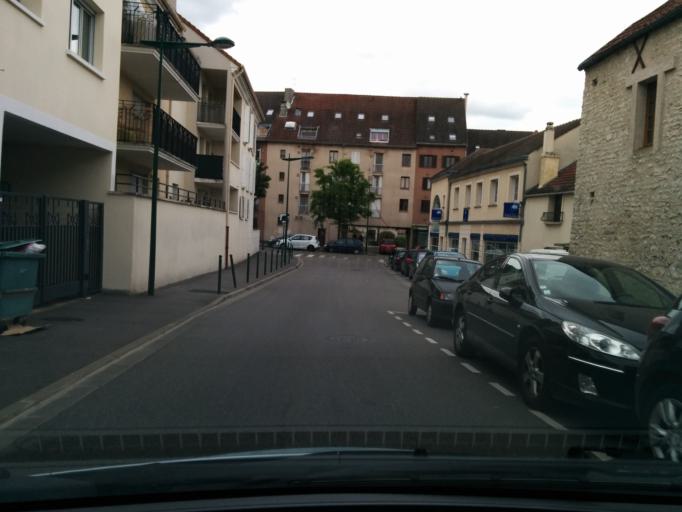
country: FR
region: Ile-de-France
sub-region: Departement des Yvelines
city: Mantes-la-Jolie
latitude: 48.9756
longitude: 1.7121
